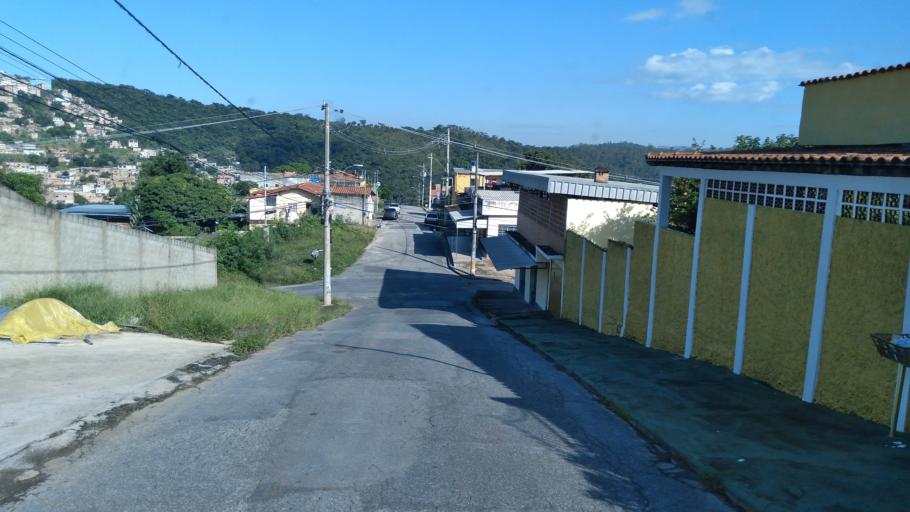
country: BR
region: Minas Gerais
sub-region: Santa Luzia
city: Santa Luzia
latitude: -19.8292
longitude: -43.8998
